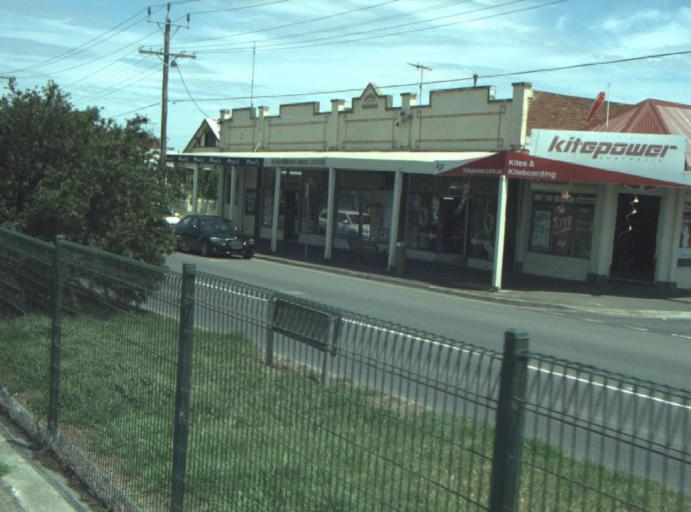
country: AU
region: Victoria
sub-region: Greater Geelong
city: Geelong
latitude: -38.1564
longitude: 144.3510
